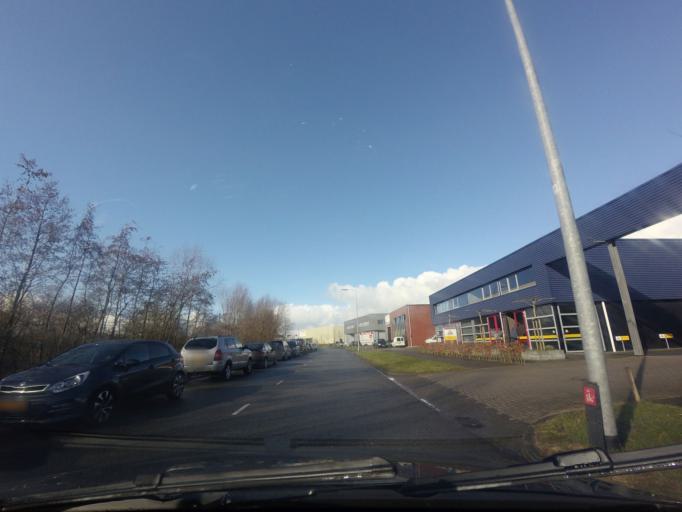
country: NL
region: Groningen
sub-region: Gemeente Groningen
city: Oosterpark
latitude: 53.2112
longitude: 6.6117
